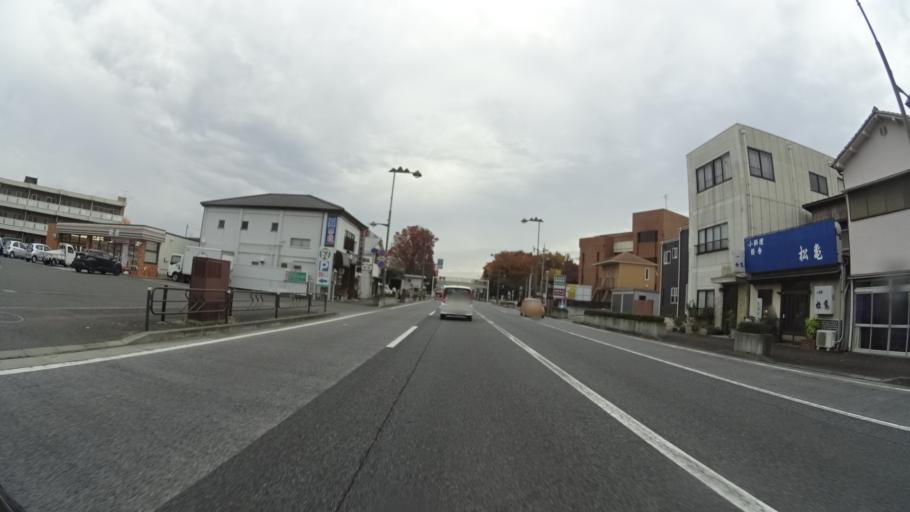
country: JP
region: Gunma
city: Maebashi-shi
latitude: 36.3833
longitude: 139.0915
